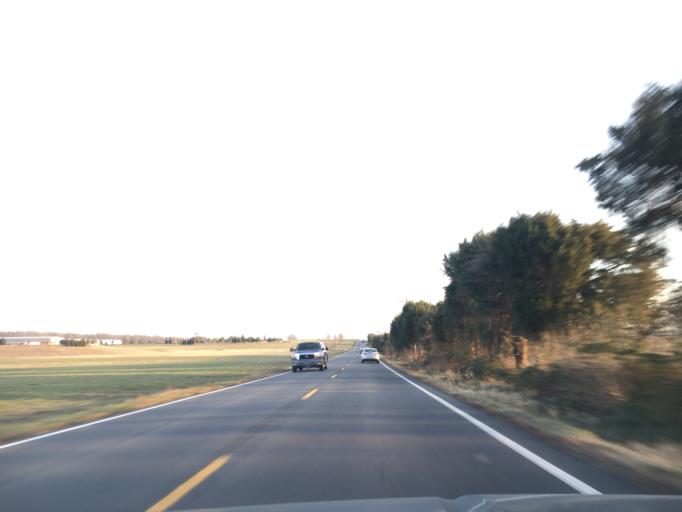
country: US
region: Virginia
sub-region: Culpeper County
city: Culpeper
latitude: 38.3833
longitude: -77.9917
